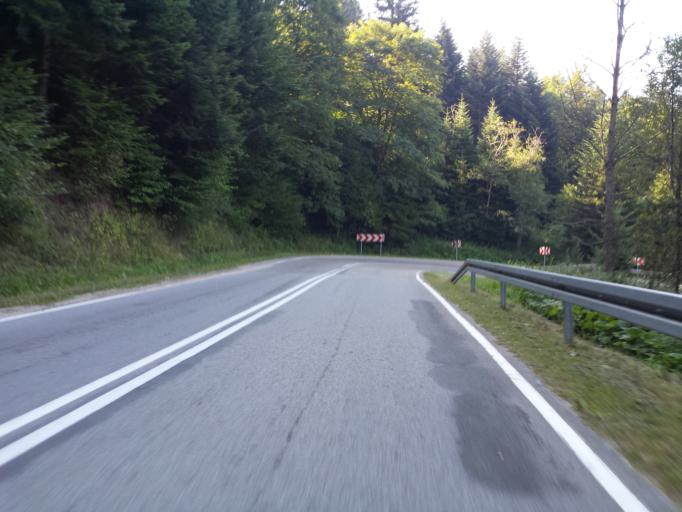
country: PL
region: Subcarpathian Voivodeship
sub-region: Powiat leski
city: Cisna
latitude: 49.2488
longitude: 22.2879
